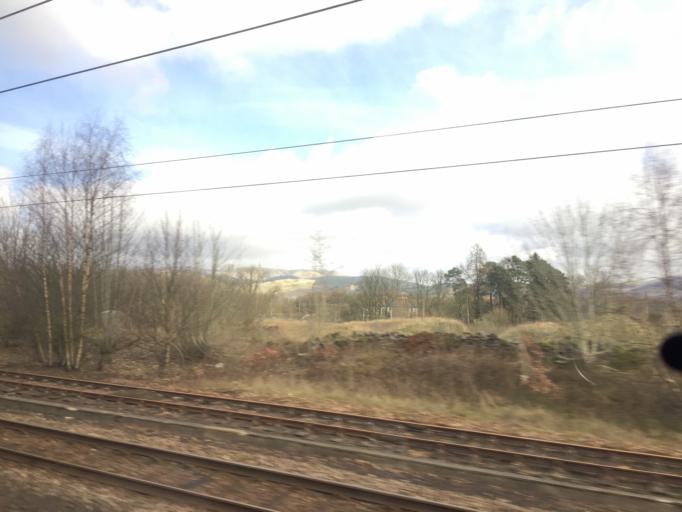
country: GB
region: Scotland
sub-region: Dumfries and Galloway
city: Moffat
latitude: 55.3090
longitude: -3.4568
